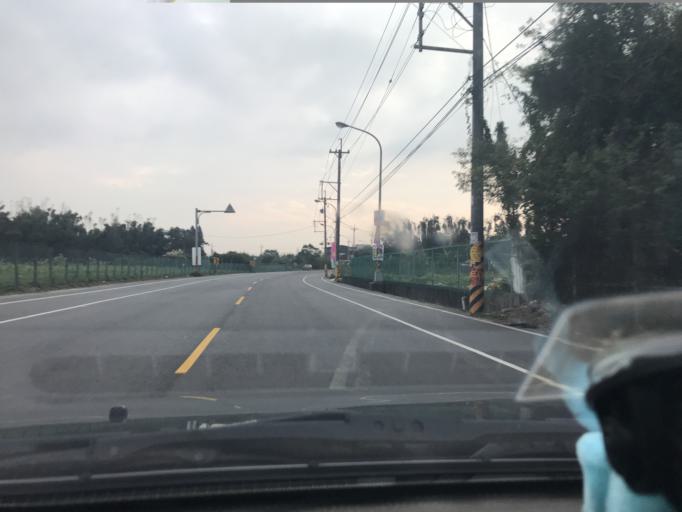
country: TW
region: Taiwan
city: Daxi
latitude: 24.8989
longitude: 121.2291
